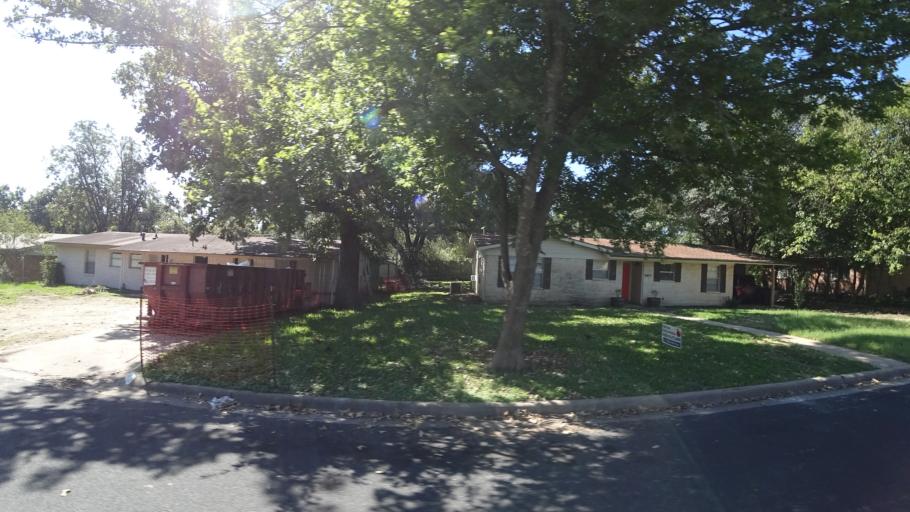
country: US
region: Texas
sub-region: Travis County
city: Austin
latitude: 30.3134
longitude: -97.6982
